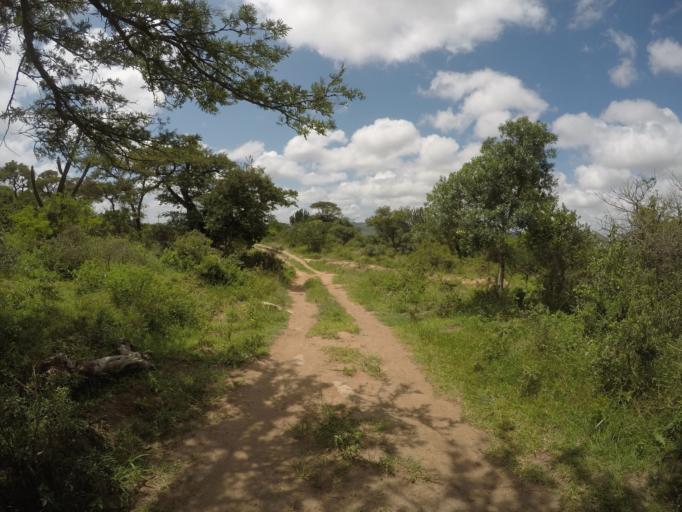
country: ZA
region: KwaZulu-Natal
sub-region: uThungulu District Municipality
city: Empangeni
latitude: -28.5860
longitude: 31.8303
